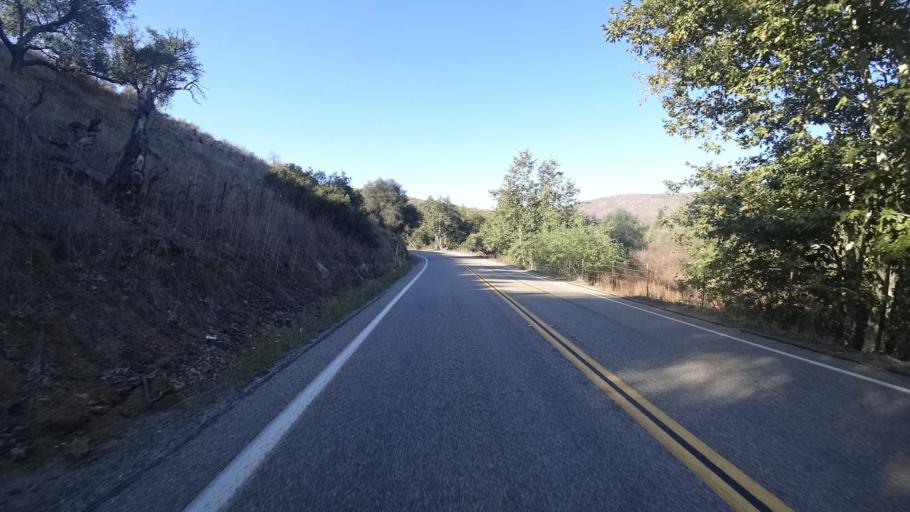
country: US
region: California
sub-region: San Diego County
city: Jamul
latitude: 32.6516
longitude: -116.8611
